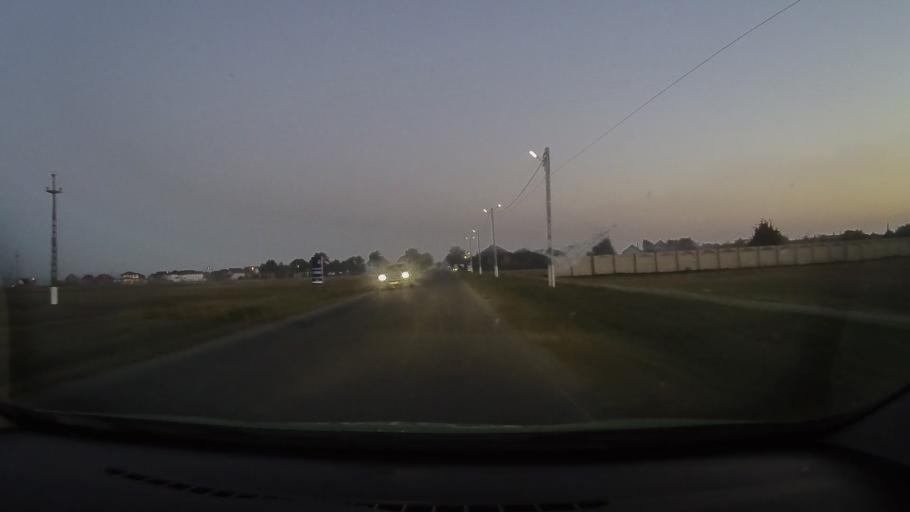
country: RO
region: Arad
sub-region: Comuna Livada
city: Livada
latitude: 46.2144
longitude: 21.3871
